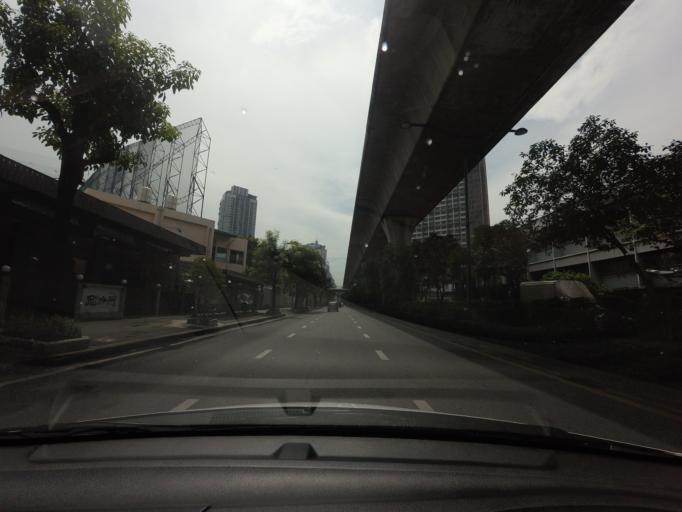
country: TH
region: Bangkok
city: Watthana
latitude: 13.7170
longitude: 100.5886
